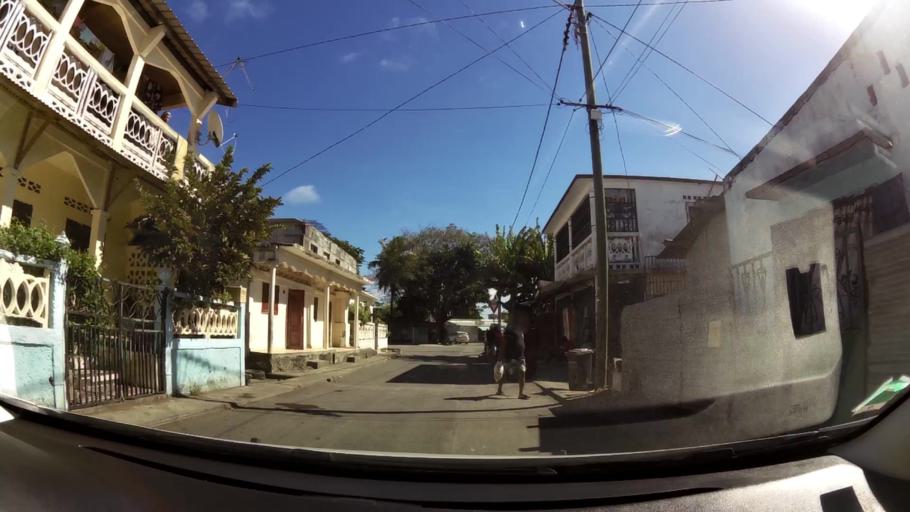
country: YT
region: Pamandzi
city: Pamandzi
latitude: -12.7866
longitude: 45.2753
